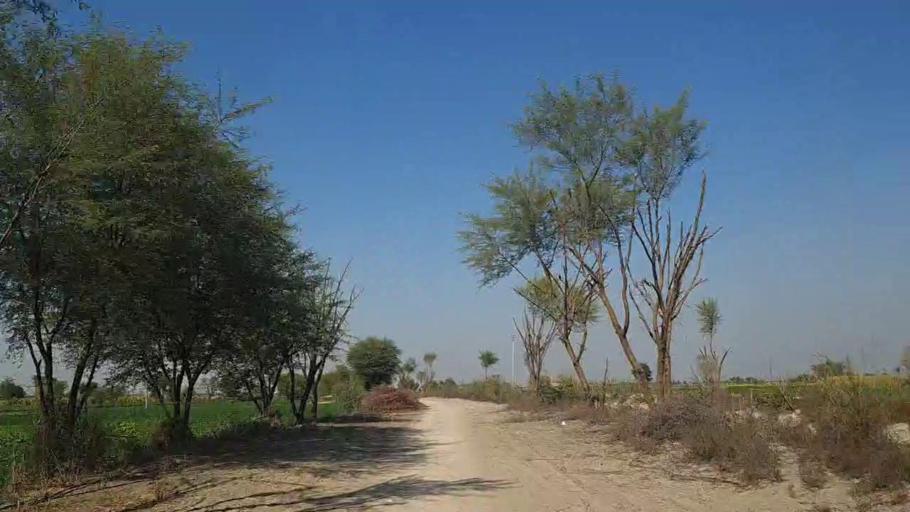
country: PK
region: Sindh
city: Sakrand
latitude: 26.2710
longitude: 68.2209
